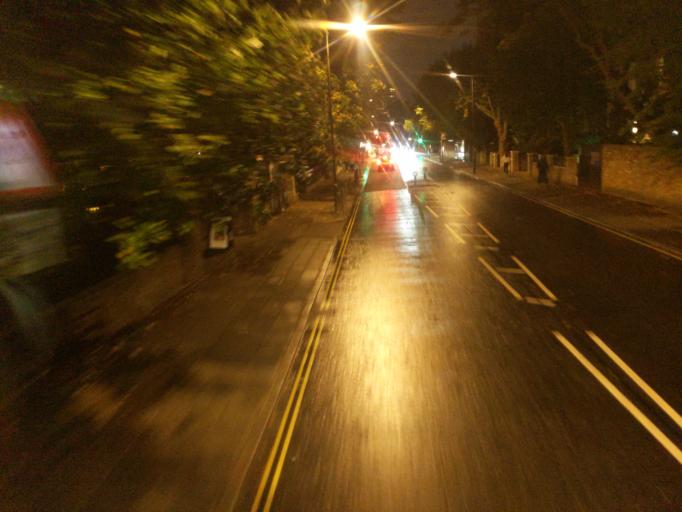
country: GB
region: England
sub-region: Greater London
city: Belsize Park
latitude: 51.5354
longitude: -0.1813
